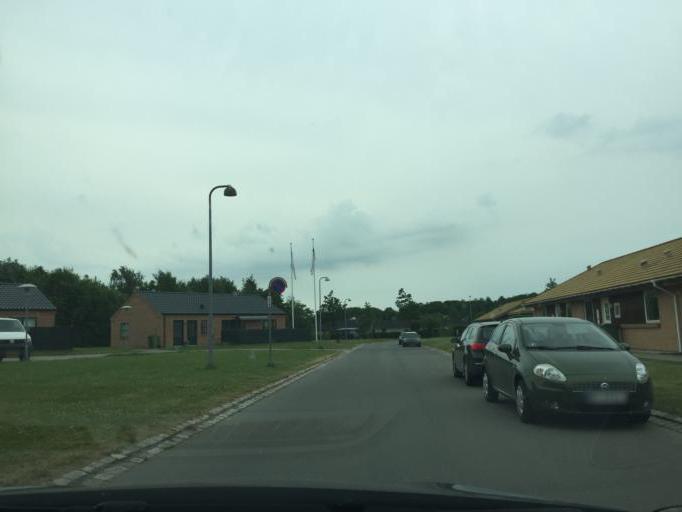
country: DK
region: South Denmark
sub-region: Odense Kommune
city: Neder Holluf
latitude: 55.3645
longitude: 10.4706
